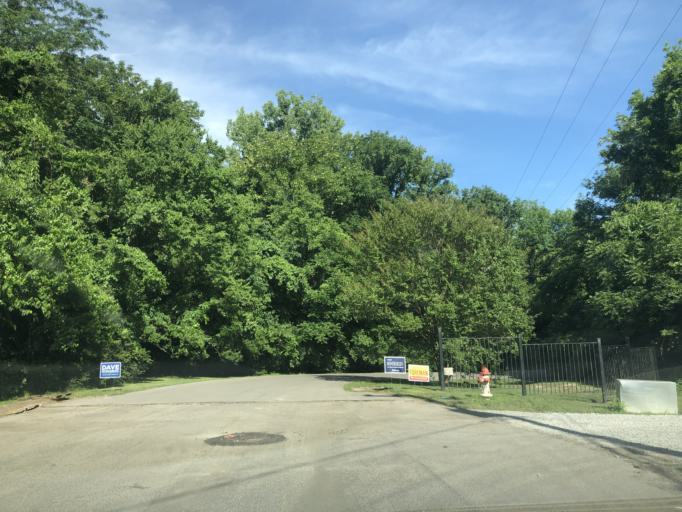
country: US
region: Tennessee
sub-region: Davidson County
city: Belle Meade
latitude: 36.0601
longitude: -86.9319
